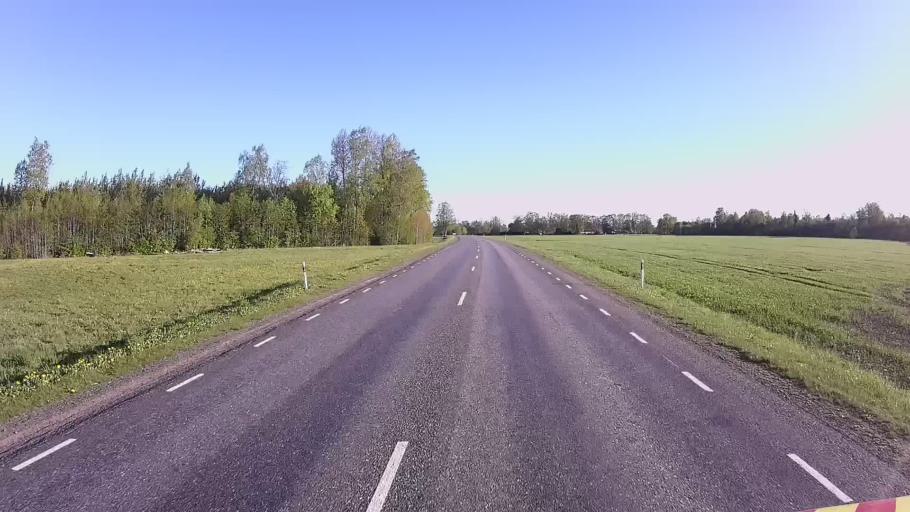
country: EE
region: Viljandimaa
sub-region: Viljandi linn
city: Viljandi
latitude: 58.4694
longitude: 25.5947
